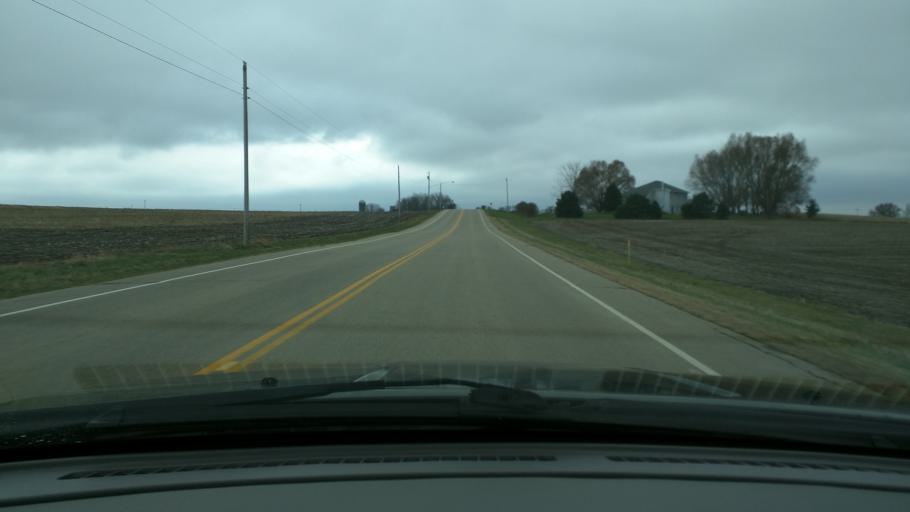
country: US
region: Minnesota
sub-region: Washington County
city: Cottage Grove
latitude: 44.7604
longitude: -92.9239
